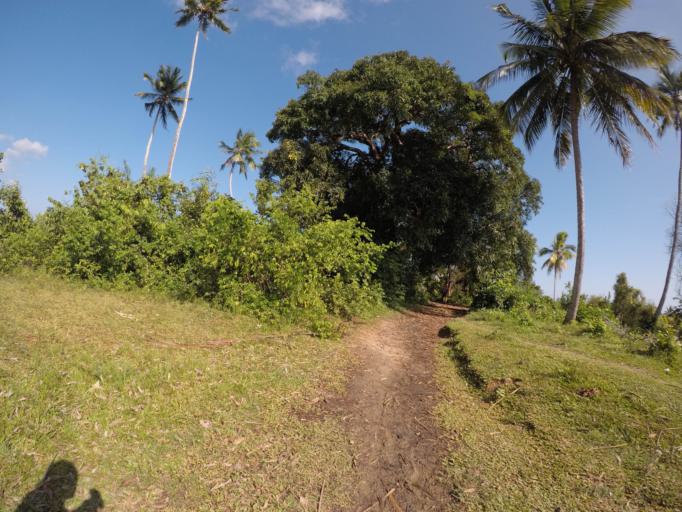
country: TZ
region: Pemba South
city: Mtambile
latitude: -5.3863
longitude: 39.7253
